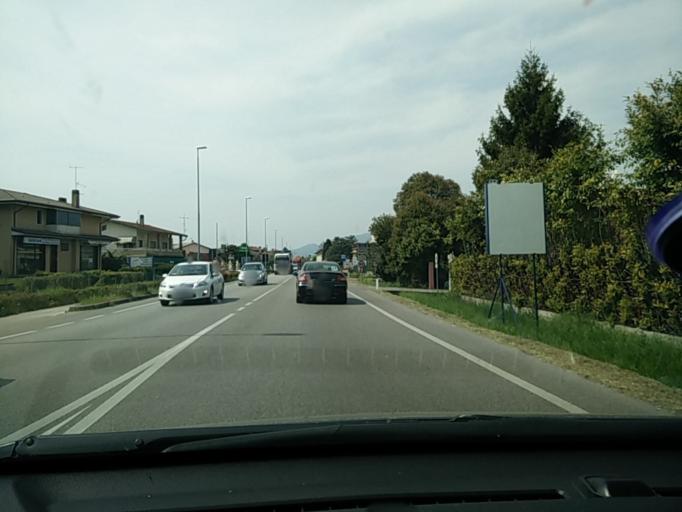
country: IT
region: Friuli Venezia Giulia
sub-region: Provincia di Pordenone
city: Vigonovo-Fontanafredda
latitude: 45.9716
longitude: 12.5754
